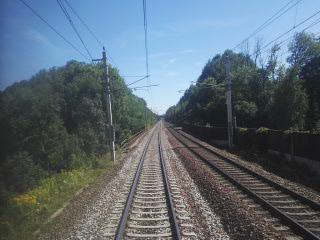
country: AT
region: Upper Austria
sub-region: Politischer Bezirk Grieskirchen
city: Bad Schallerbach
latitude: 48.2250
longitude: 13.9367
